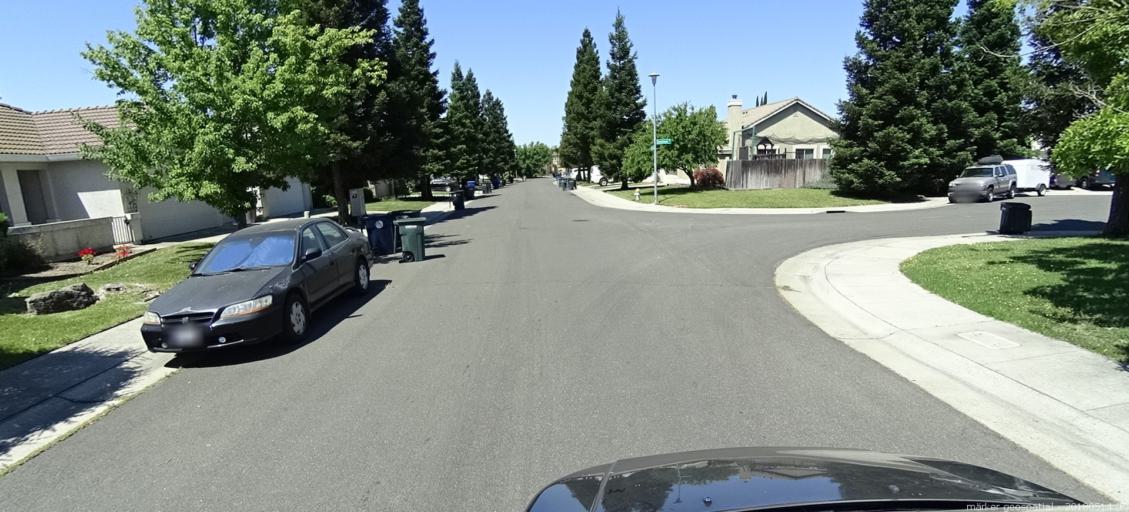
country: US
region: California
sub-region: Yolo County
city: West Sacramento
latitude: 38.6337
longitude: -121.5295
